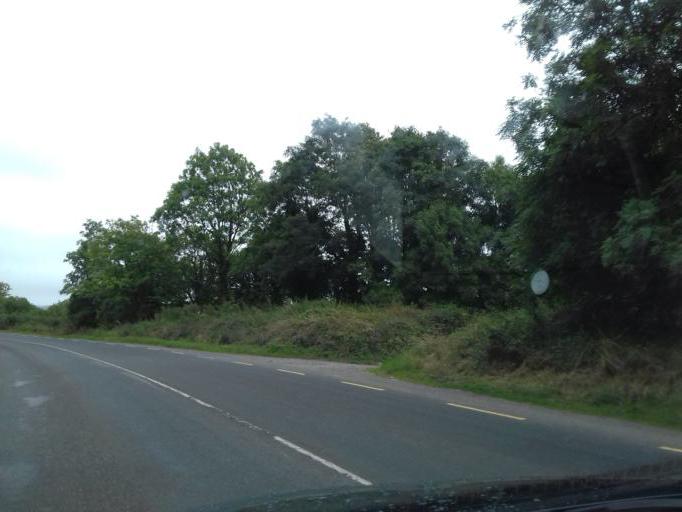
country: IE
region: Leinster
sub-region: County Carlow
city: Bagenalstown
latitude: 52.6272
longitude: -7.0230
